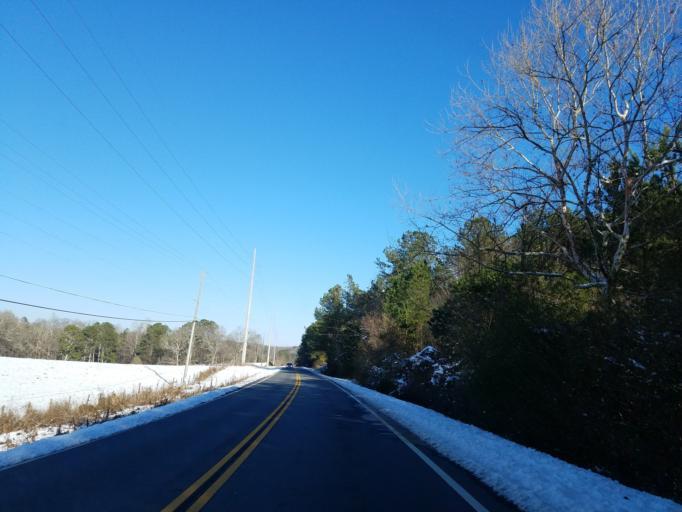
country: US
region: Georgia
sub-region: Dawson County
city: Dawsonville
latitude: 34.3492
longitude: -84.1074
